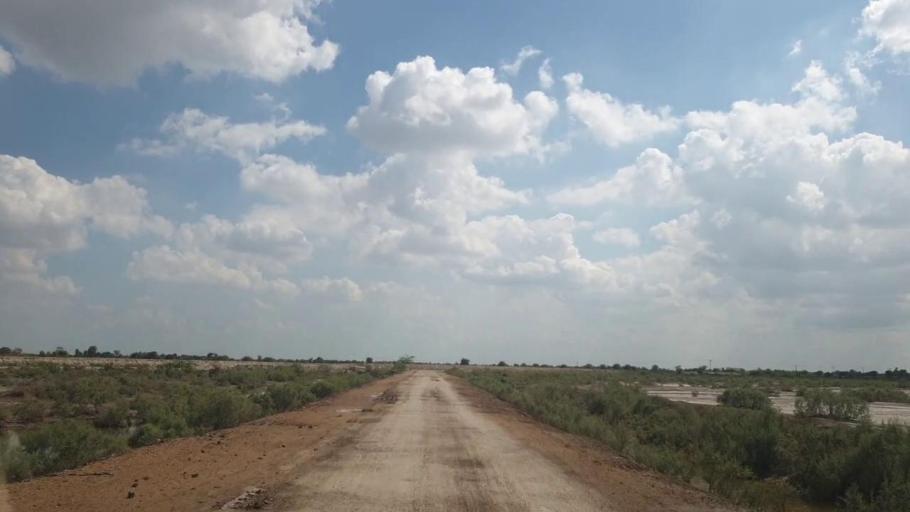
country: PK
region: Sindh
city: Pithoro
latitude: 25.5945
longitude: 69.4009
